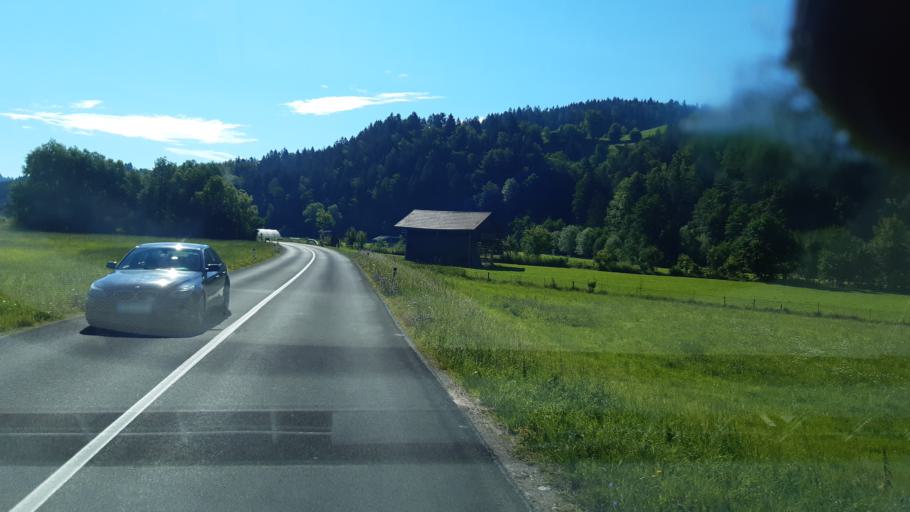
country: SI
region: Lukovica
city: Lukovica pri Domzalah
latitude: 46.2182
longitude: 14.7536
